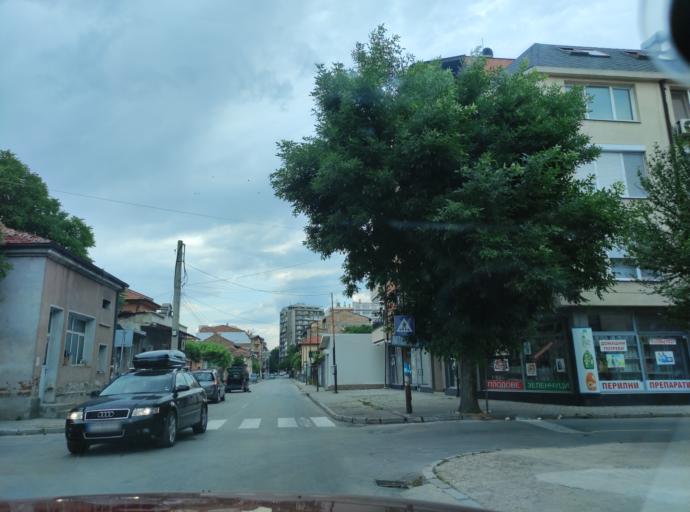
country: BG
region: Pazardzhik
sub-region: Obshtina Pazardzhik
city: Pazardzhik
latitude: 42.1839
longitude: 24.3350
